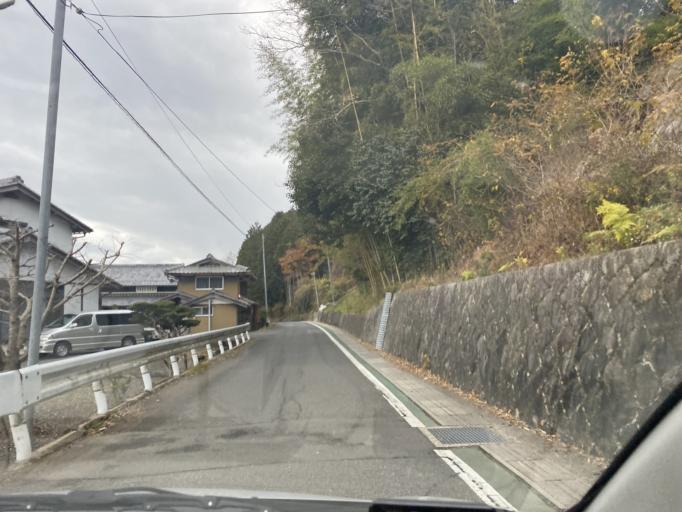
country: JP
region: Kyoto
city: Kameoka
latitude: 35.0515
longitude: 135.4774
